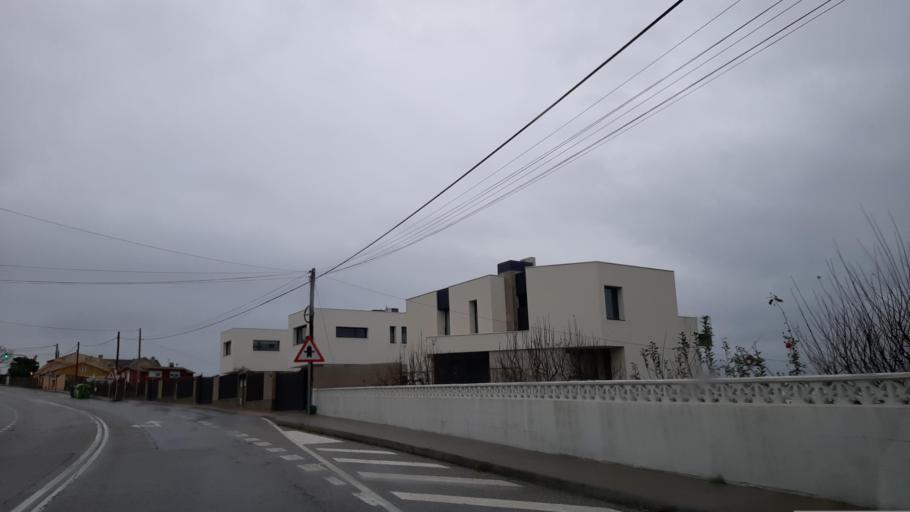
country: ES
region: Galicia
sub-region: Provincia de Pontevedra
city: Nigran
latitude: 42.1789
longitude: -8.7988
